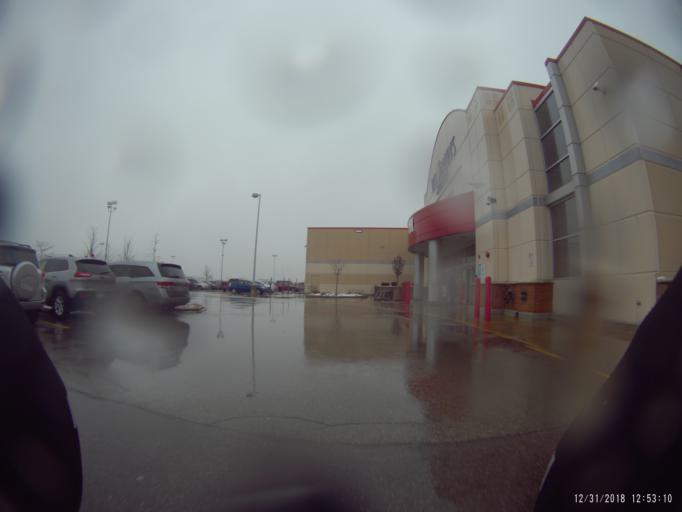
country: US
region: Wisconsin
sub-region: Dane County
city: Middleton
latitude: 43.0493
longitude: -89.5006
